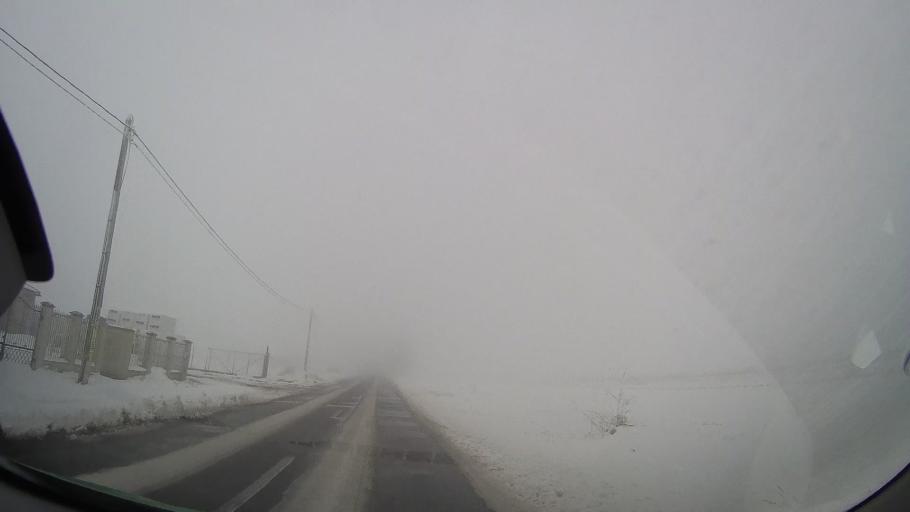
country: RO
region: Neamt
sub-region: Comuna Sabaoani
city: Sabaoani
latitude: 47.0290
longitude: 26.8591
